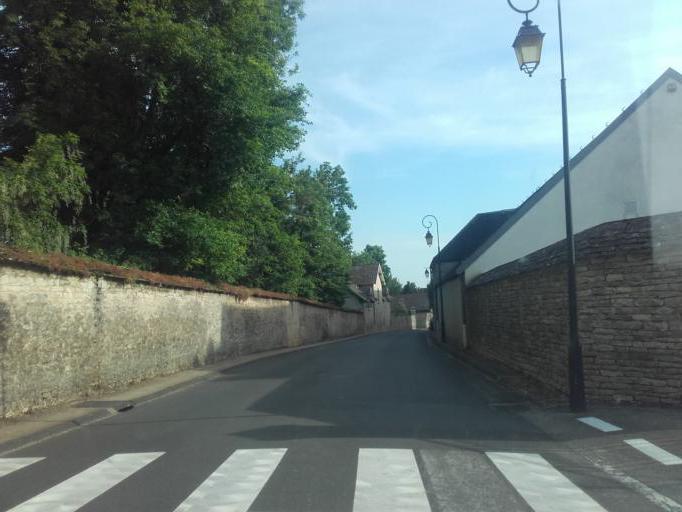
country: FR
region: Bourgogne
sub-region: Departement de la Cote-d'Or
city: Meursault
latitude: 46.9839
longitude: 4.7686
